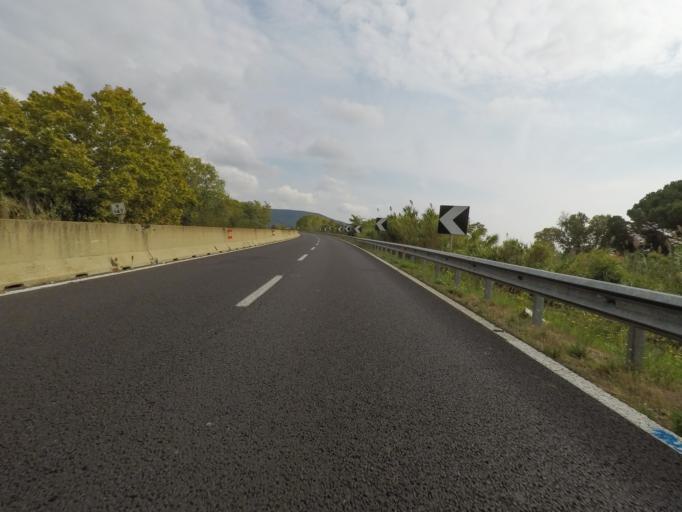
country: IT
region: Tuscany
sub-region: Provincia di Grosseto
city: Albinia
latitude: 42.4798
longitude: 11.2232
